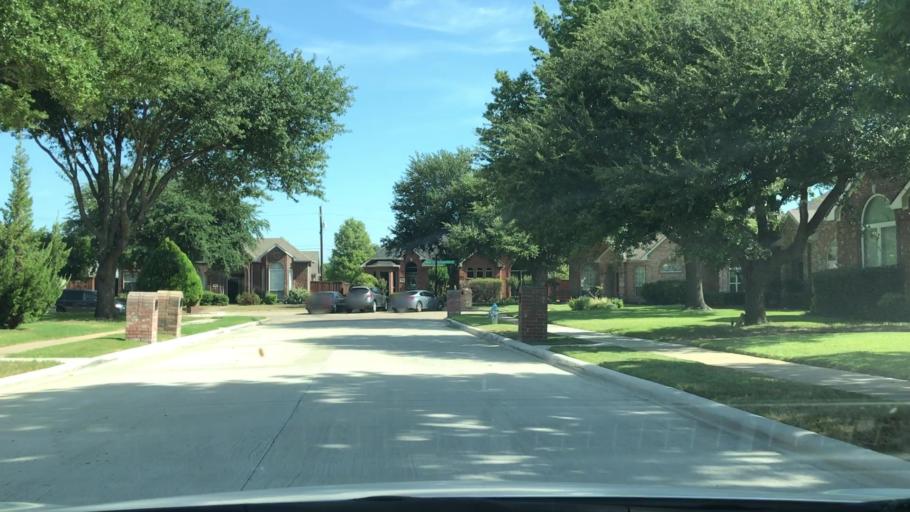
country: US
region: Texas
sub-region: Collin County
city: Plano
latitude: 33.0553
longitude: -96.7650
